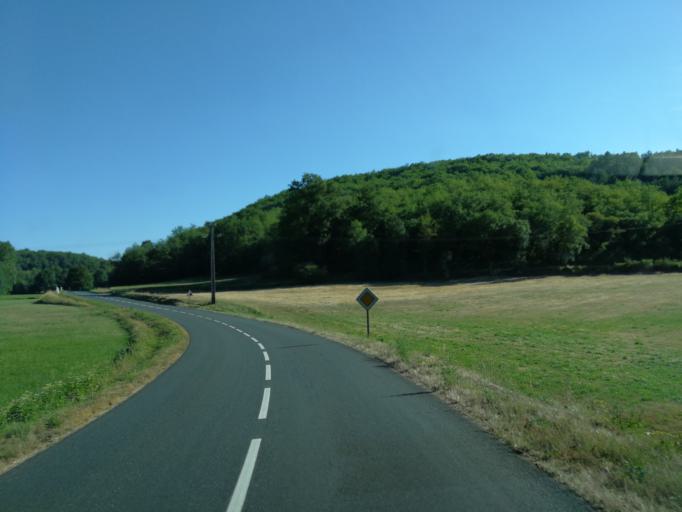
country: FR
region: Midi-Pyrenees
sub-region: Departement du Lot
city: Salviac
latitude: 44.7020
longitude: 1.2962
